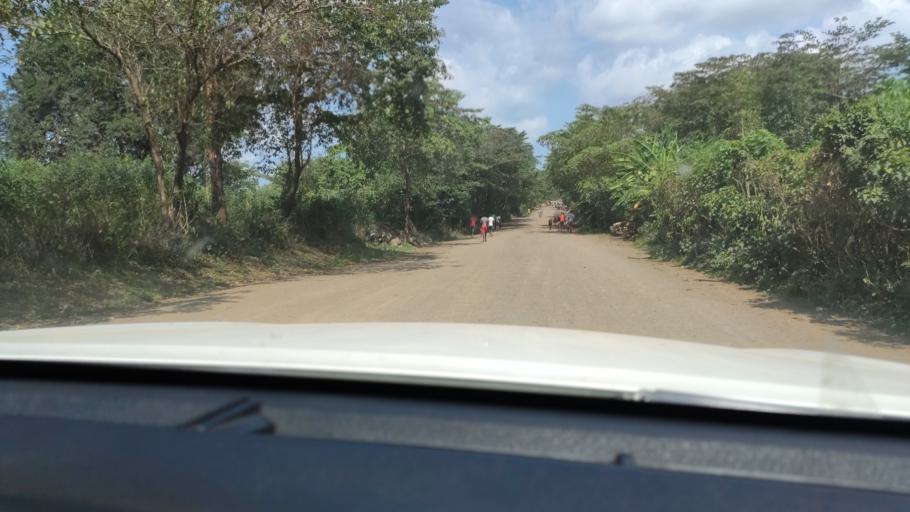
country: ET
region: Southern Nations, Nationalities, and People's Region
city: Felege Neway
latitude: 6.3958
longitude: 37.0785
